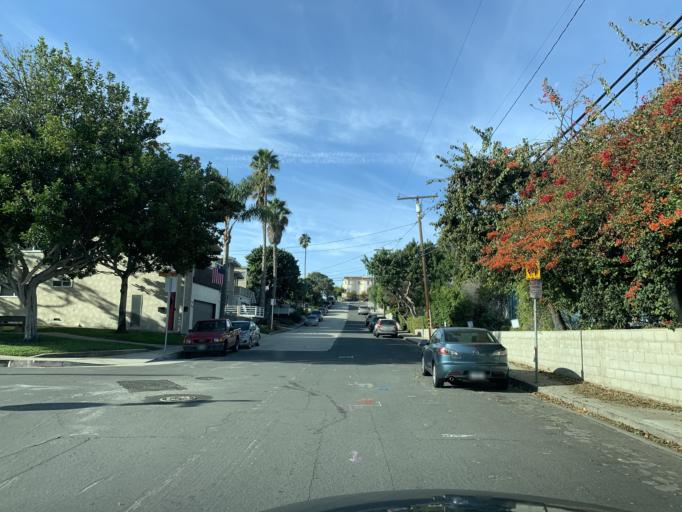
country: US
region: California
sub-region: Los Angeles County
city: Manhattan Beach
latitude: 33.8777
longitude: -118.4030
